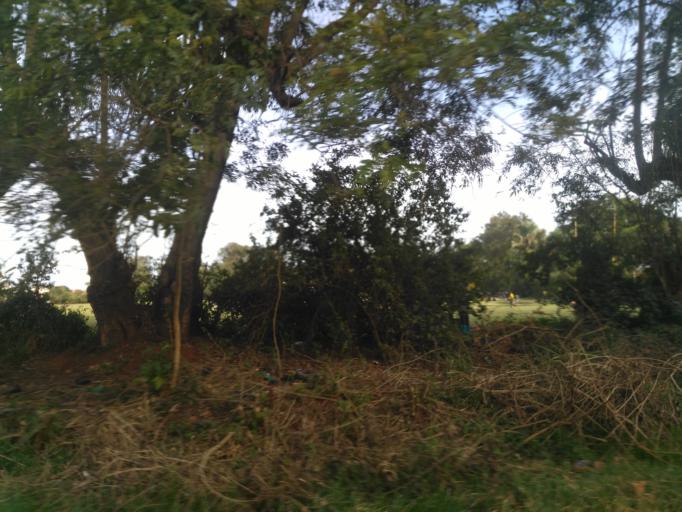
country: UG
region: Eastern Region
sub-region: Jinja District
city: Jinja
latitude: 0.4232
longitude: 33.2007
